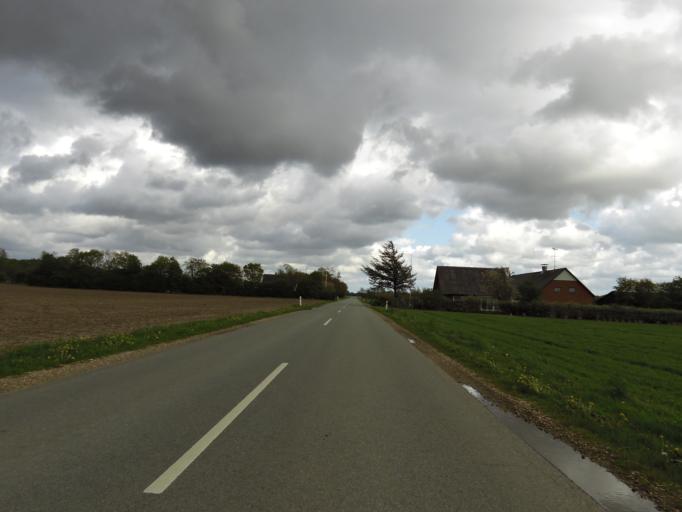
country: DK
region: South Denmark
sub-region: Haderslev Kommune
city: Gram
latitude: 55.3023
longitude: 9.0362
